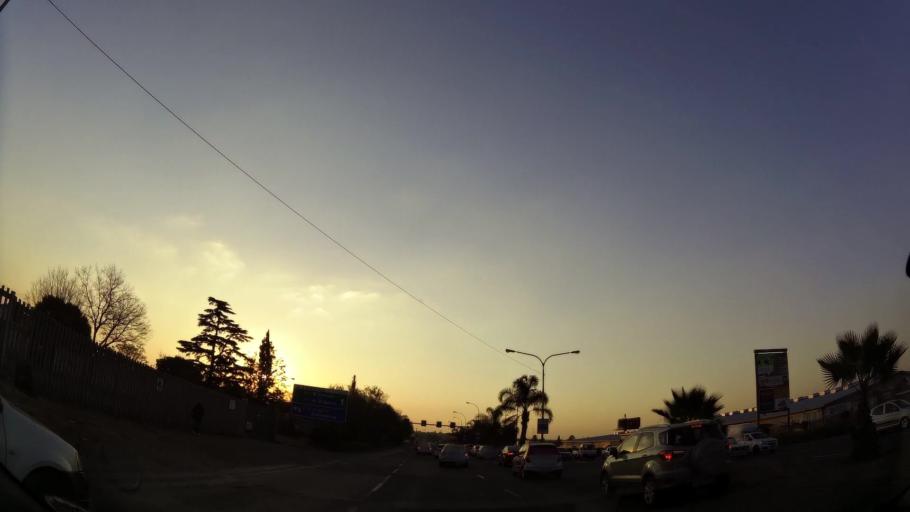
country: ZA
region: Gauteng
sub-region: City of Johannesburg Metropolitan Municipality
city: Modderfontein
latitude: -26.1584
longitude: 28.1649
